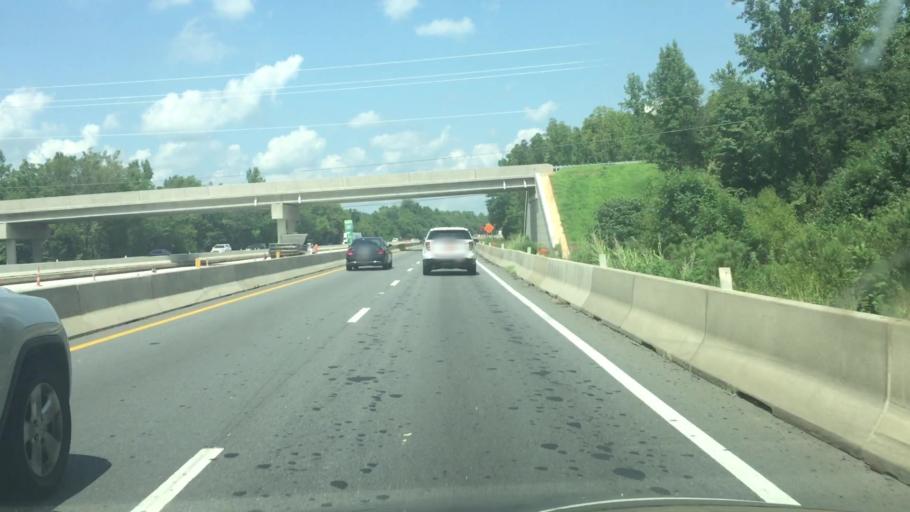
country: US
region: North Carolina
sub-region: Rowan County
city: China Grove
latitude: 35.5528
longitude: -80.5706
